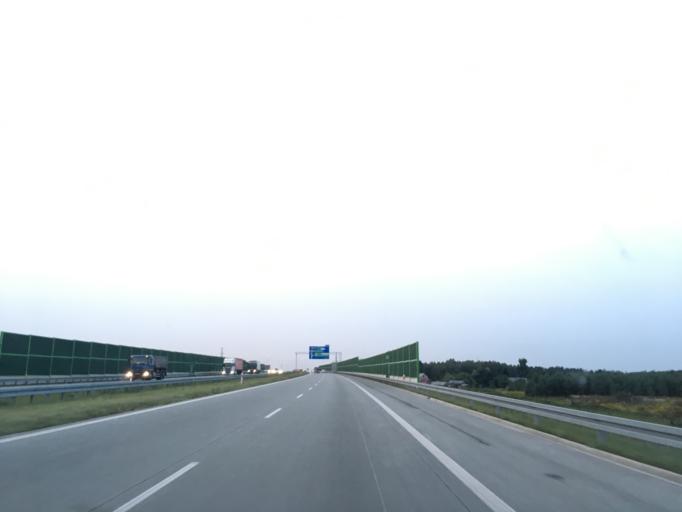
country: PL
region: Lodz Voivodeship
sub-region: Powiat lodzki wschodni
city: Andrespol
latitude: 51.7578
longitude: 19.5951
